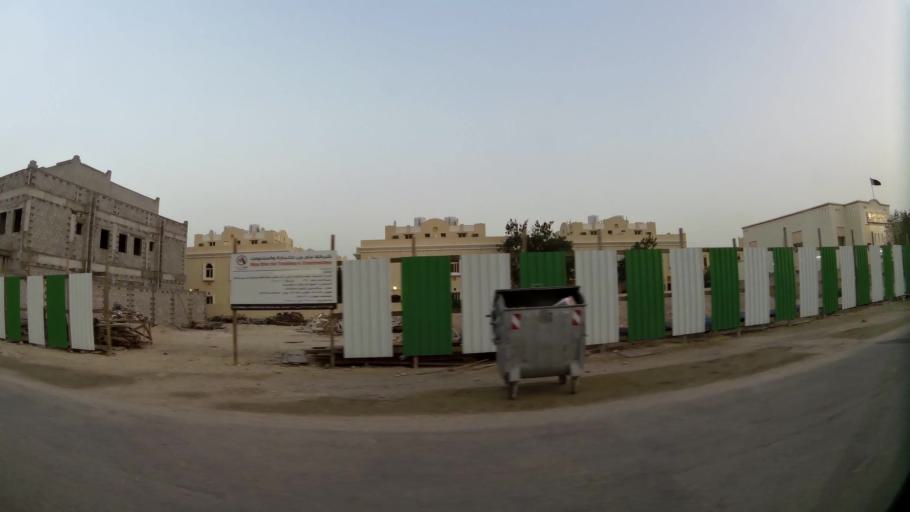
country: QA
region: Baladiyat ar Rayyan
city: Ar Rayyan
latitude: 25.2503
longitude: 51.4615
